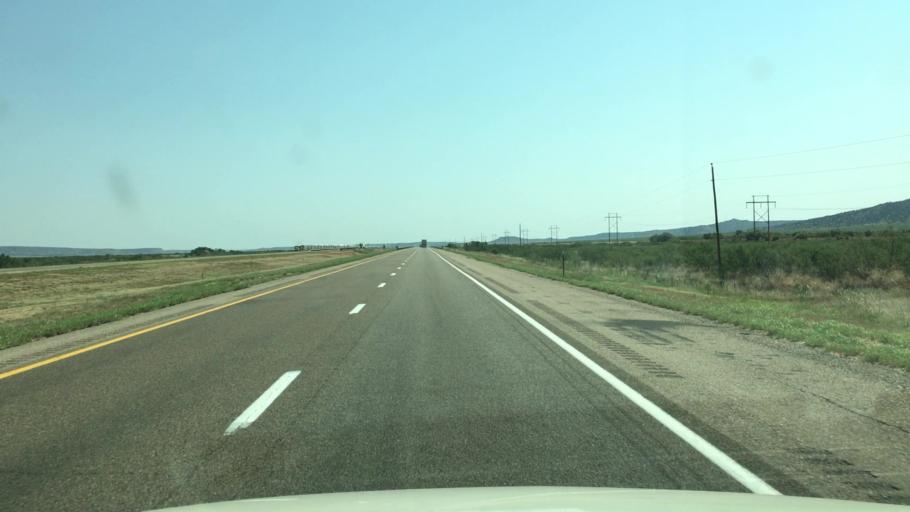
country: US
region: New Mexico
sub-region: Quay County
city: Tucumcari
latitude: 35.1053
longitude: -104.0280
